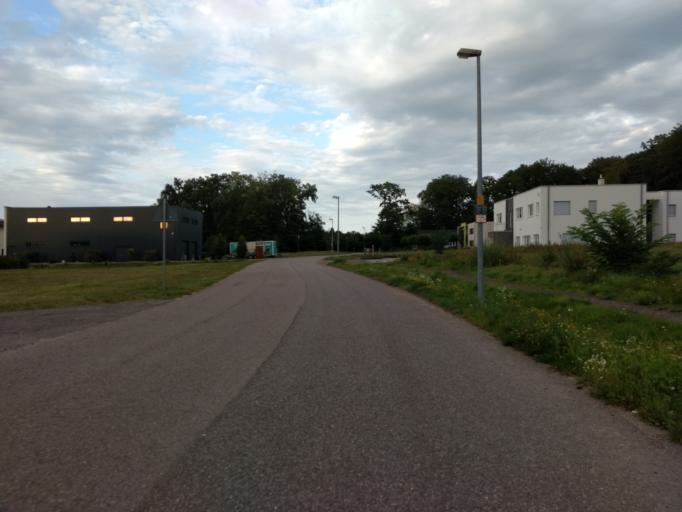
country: DE
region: Saarland
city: Saarwellingen
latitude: 49.3566
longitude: 6.7790
